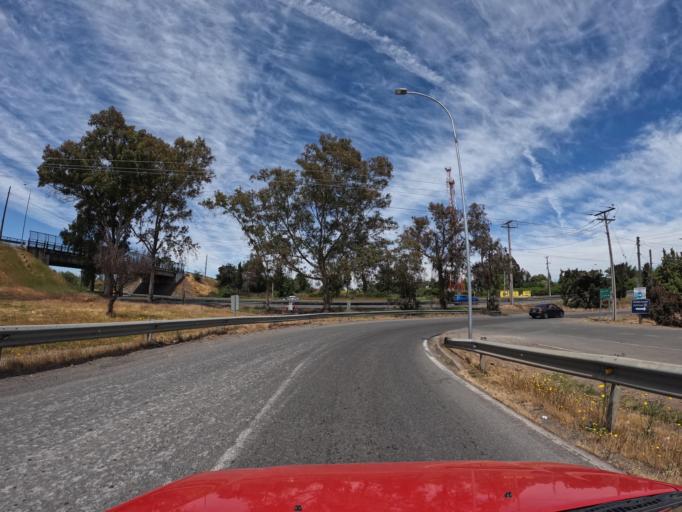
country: CL
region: Maule
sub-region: Provincia de Talca
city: Talca
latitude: -35.3033
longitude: -71.5191
